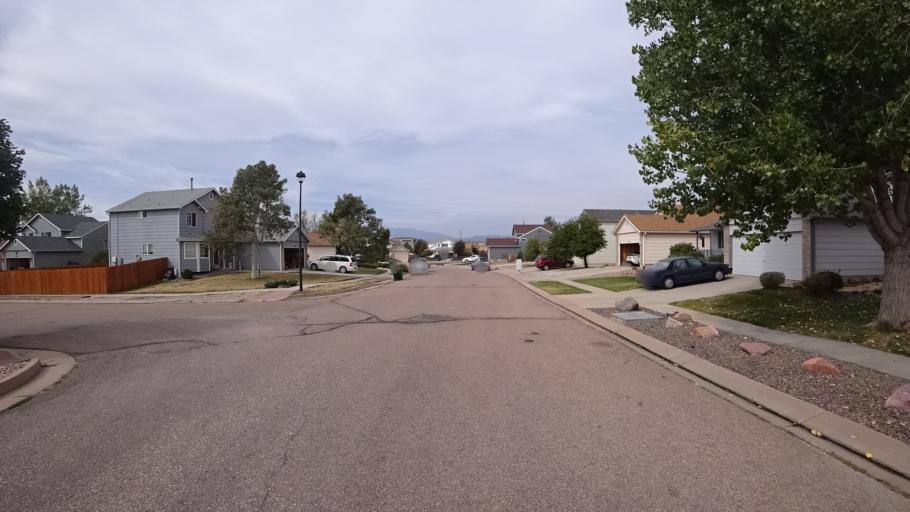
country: US
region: Colorado
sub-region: El Paso County
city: Cimarron Hills
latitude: 38.9165
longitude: -104.7153
